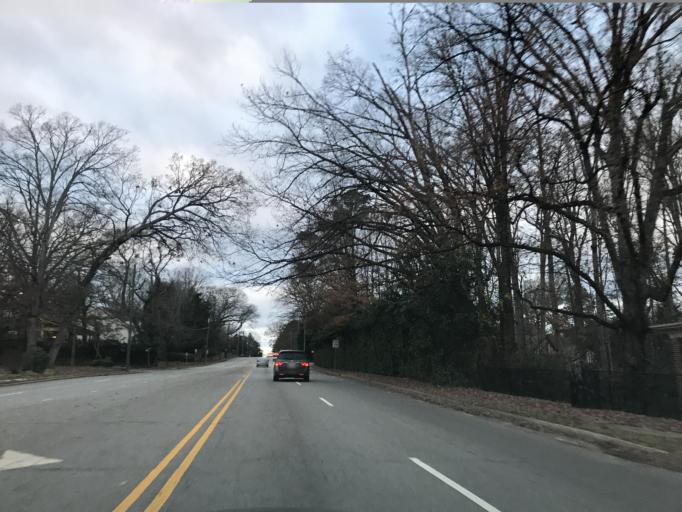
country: US
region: North Carolina
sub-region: Wake County
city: West Raleigh
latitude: 35.8094
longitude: -78.6490
